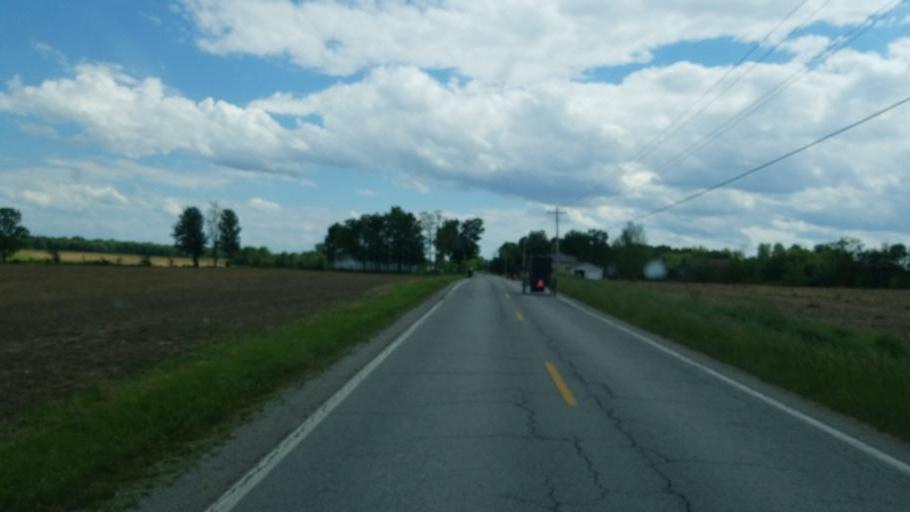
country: US
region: Ohio
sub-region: Huron County
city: Plymouth
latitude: 41.0492
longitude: -82.6094
